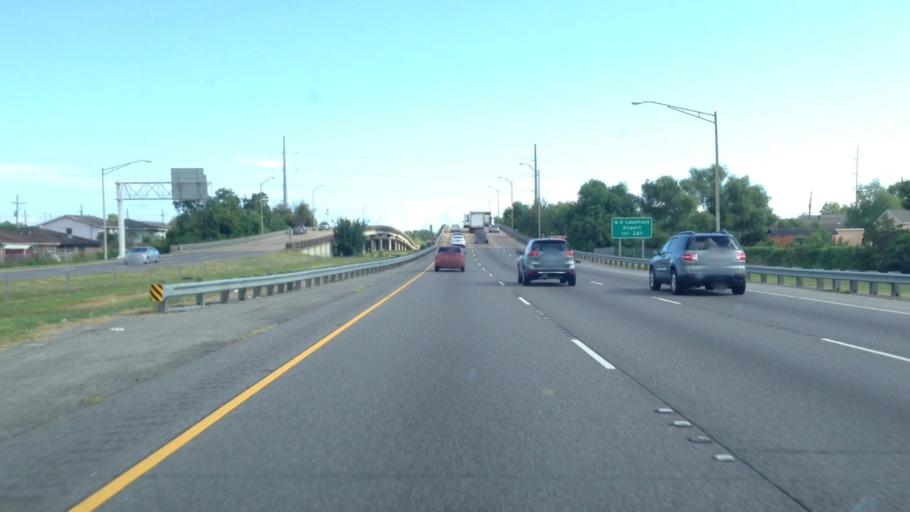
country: US
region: Louisiana
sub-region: Saint Bernard Parish
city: Arabi
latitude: 30.0177
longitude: -90.0135
